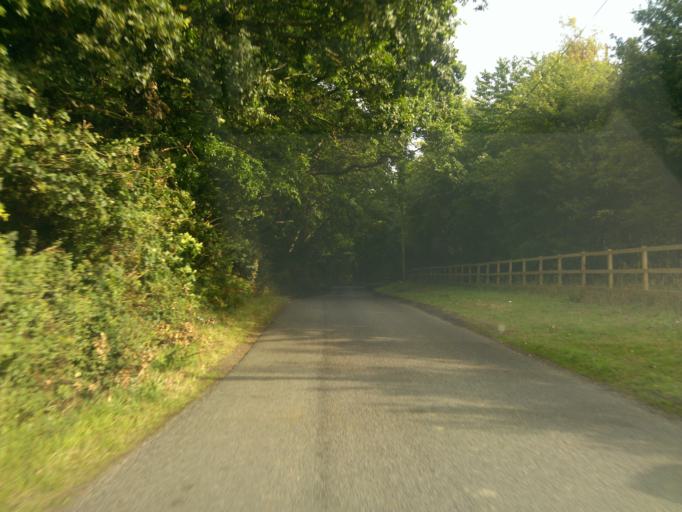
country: GB
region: England
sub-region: Essex
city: Saint Osyth
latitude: 51.8324
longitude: 1.1032
